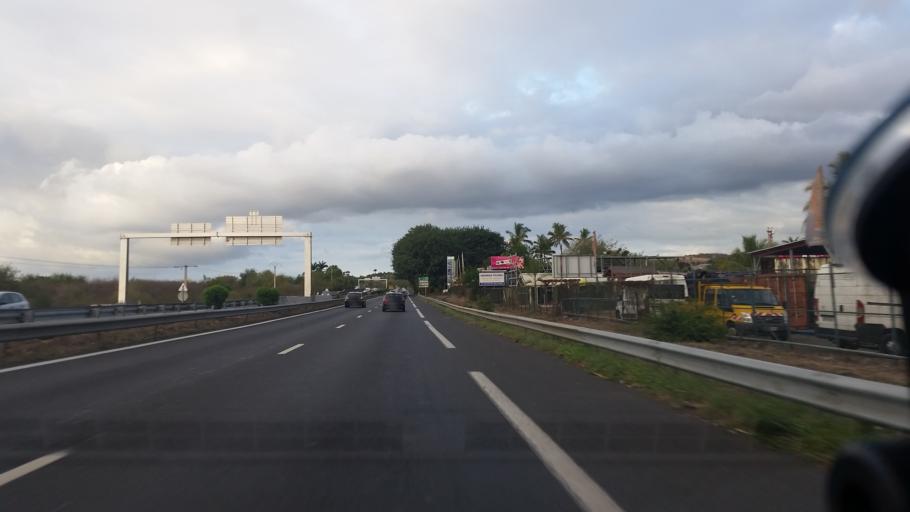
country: RE
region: Reunion
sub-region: Reunion
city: Saint-Paul
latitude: -20.9799
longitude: 55.2950
